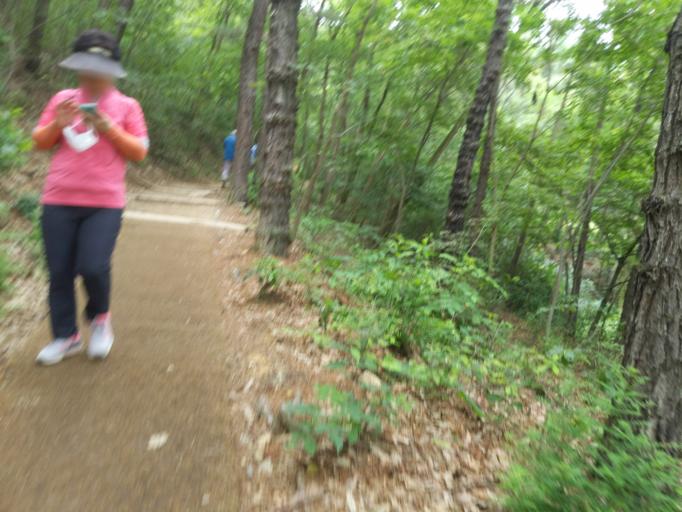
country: KR
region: Daegu
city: Hwawon
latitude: 35.7944
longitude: 128.5260
